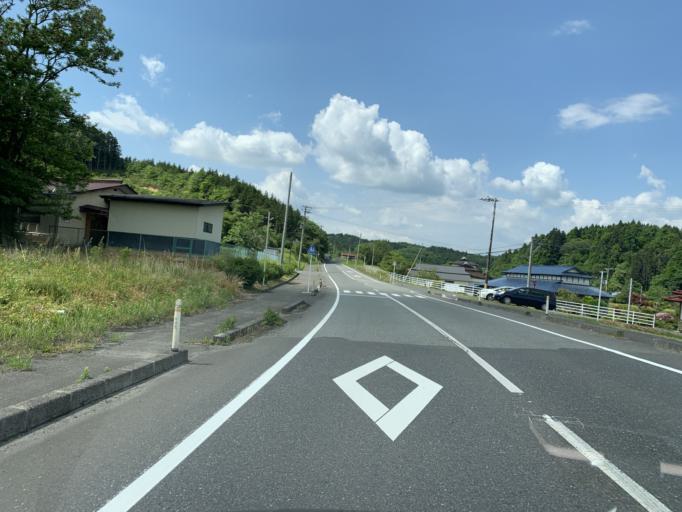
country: JP
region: Miyagi
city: Furukawa
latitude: 38.7284
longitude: 140.9536
